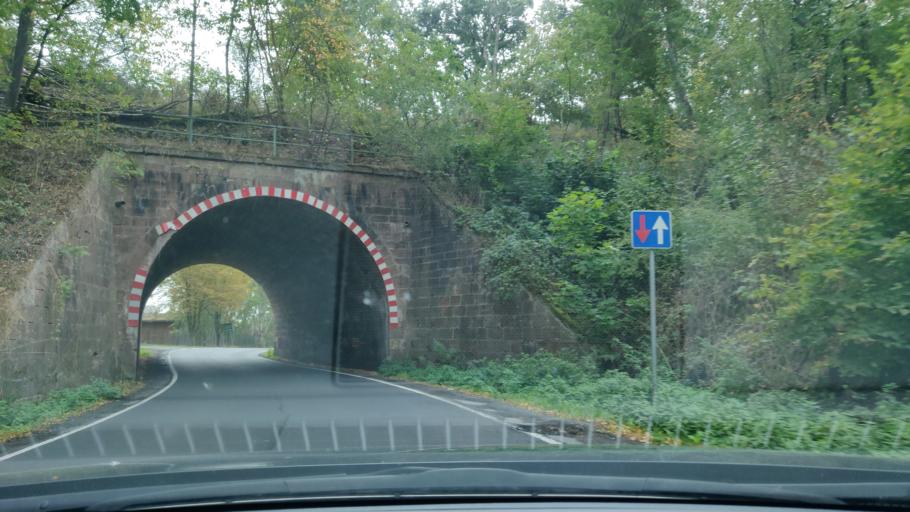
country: DE
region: Hesse
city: Schwalmstadt
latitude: 50.9261
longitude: 9.2225
